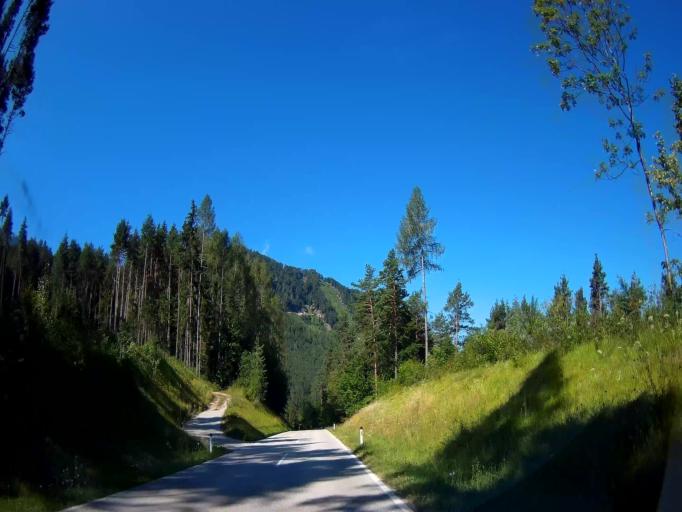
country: AT
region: Carinthia
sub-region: Politischer Bezirk Klagenfurt Land
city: Ebenthal
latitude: 46.5381
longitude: 14.4033
